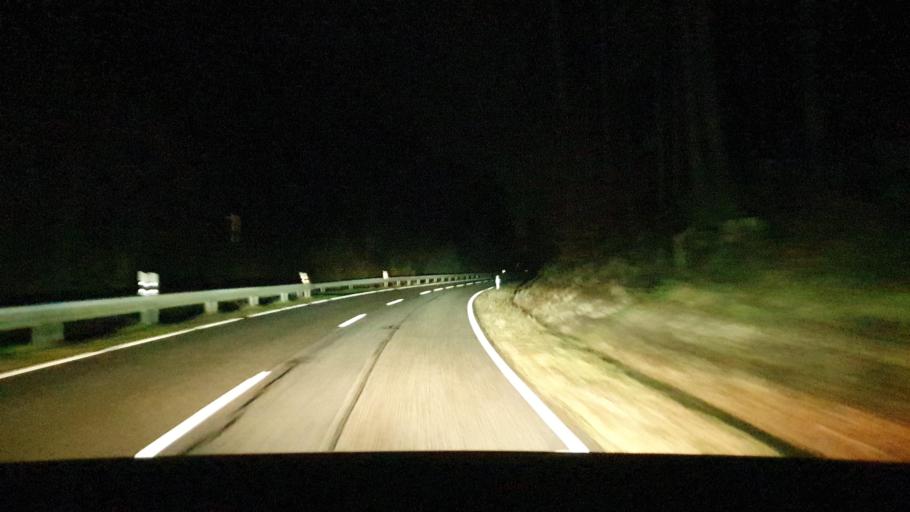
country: DE
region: Rheinland-Pfalz
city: Trippstadt
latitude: 49.3810
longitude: 7.7823
